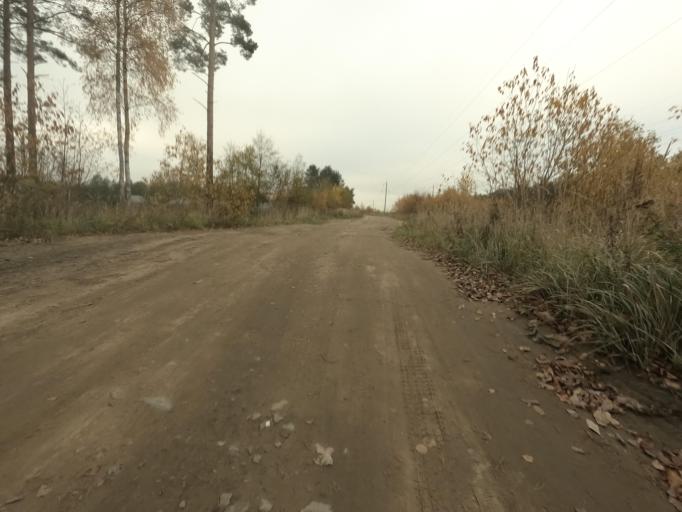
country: RU
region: Leningrad
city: Kirovsk
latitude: 59.8532
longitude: 30.9846
